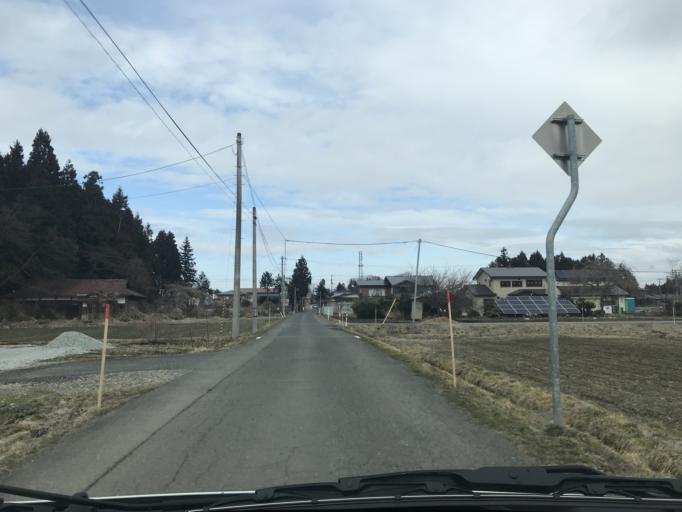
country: JP
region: Iwate
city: Kitakami
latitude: 39.3048
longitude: 141.0007
